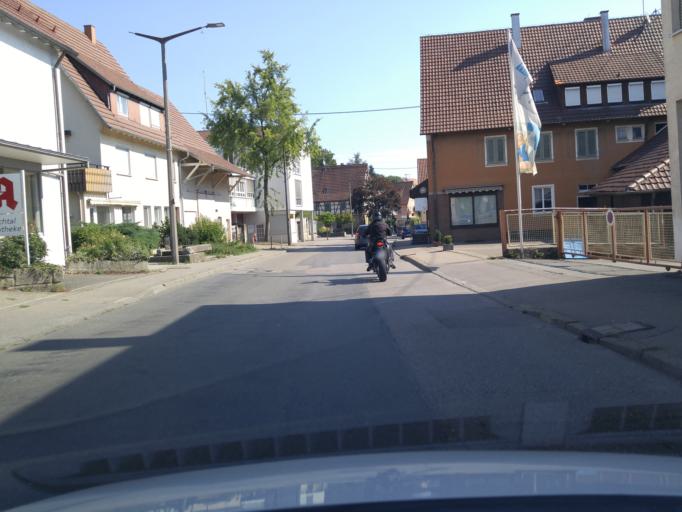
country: DE
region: Baden-Wuerttemberg
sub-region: Regierungsbezirk Stuttgart
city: Schlaitdorf
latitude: 48.6218
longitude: 9.2375
